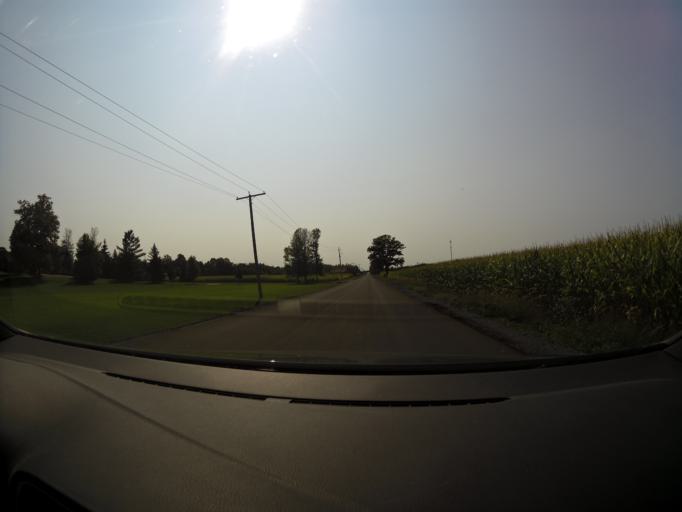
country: CA
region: Ontario
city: Carleton Place
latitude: 45.3276
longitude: -76.0917
